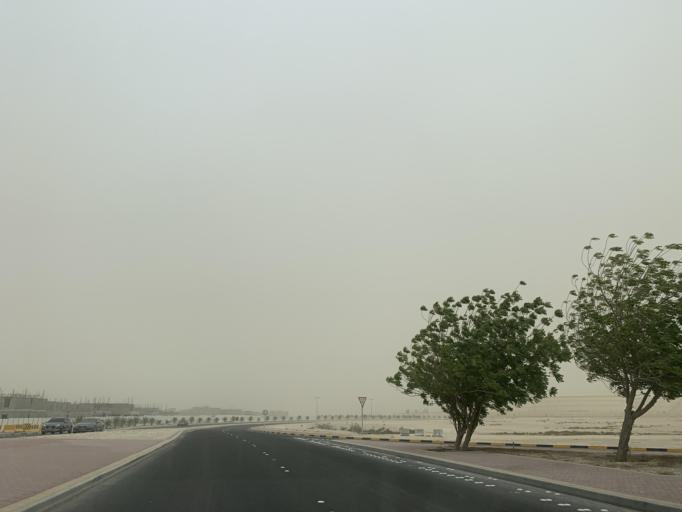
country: BH
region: Central Governorate
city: Madinat Hamad
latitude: 26.1217
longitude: 50.5081
